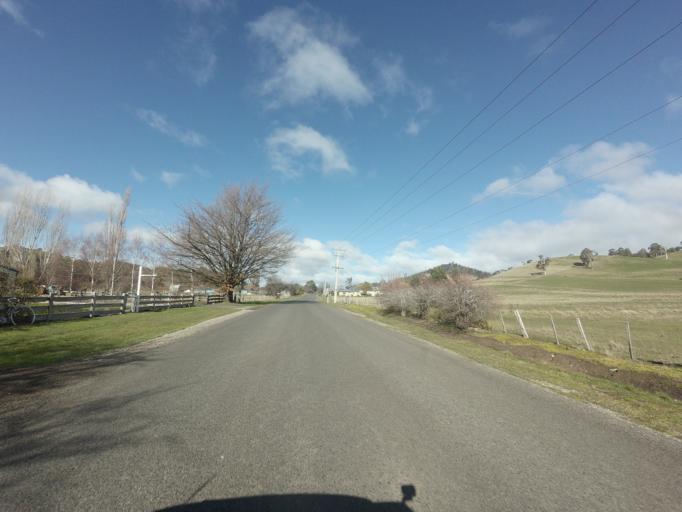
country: AU
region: Tasmania
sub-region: Derwent Valley
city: New Norfolk
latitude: -42.6124
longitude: 146.7125
